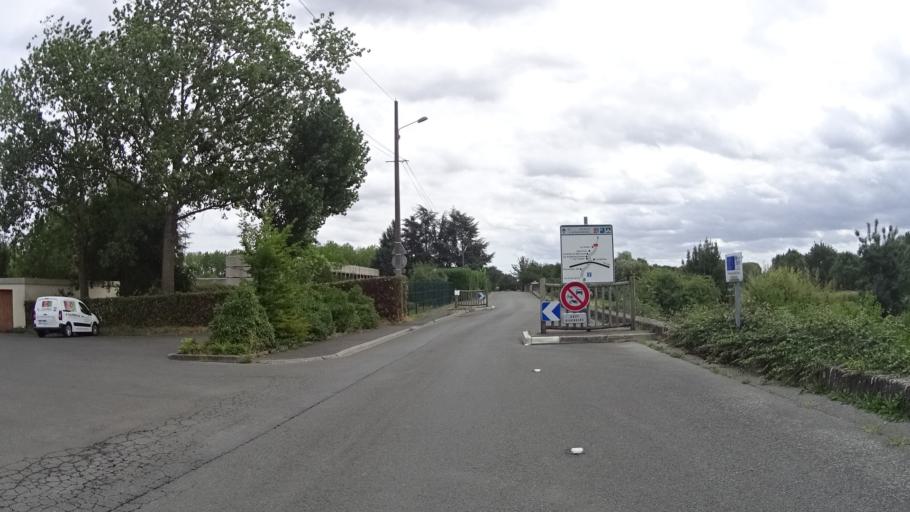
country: FR
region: Pays de la Loire
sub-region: Departement de Maine-et-Loire
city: Les Ponts-de-Ce
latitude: 47.4288
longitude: -0.5213
